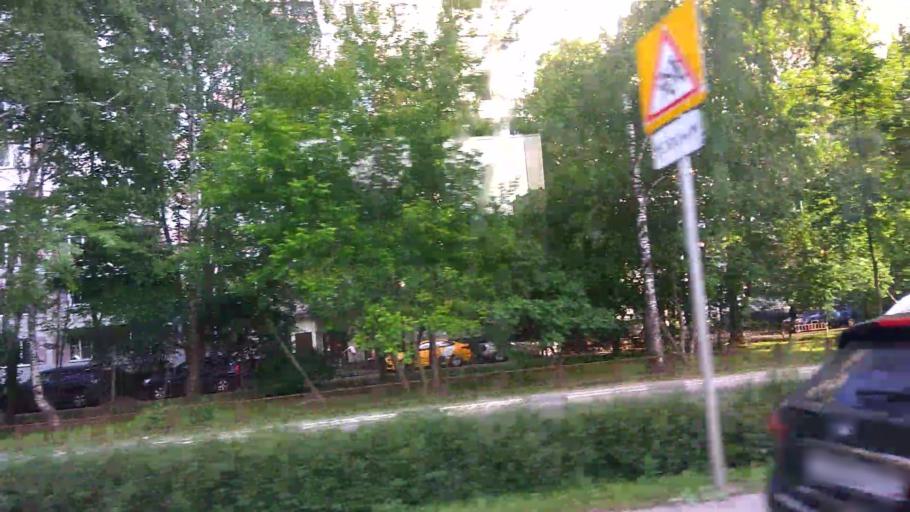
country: RU
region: Moskovskaya
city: Mytishchi
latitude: 55.9087
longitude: 37.7114
